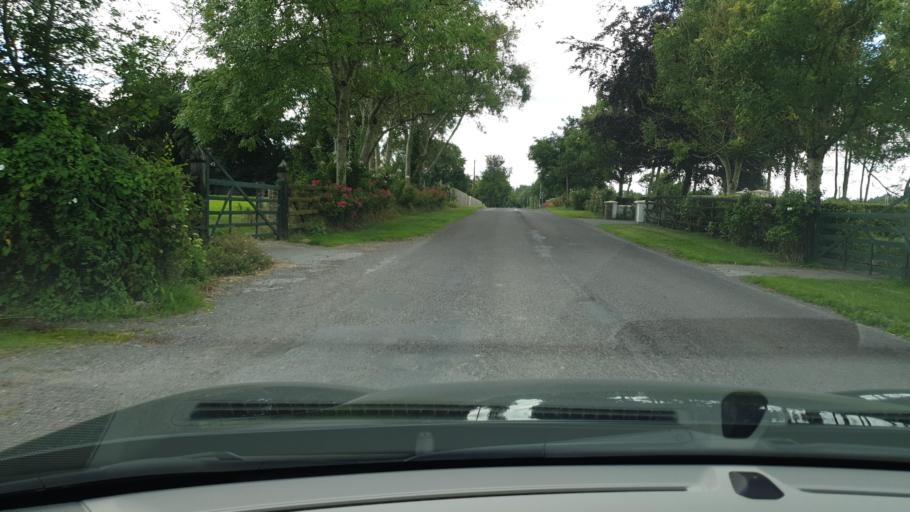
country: IE
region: Leinster
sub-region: An Mhi
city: Dunshaughlin
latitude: 53.5669
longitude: -6.5799
